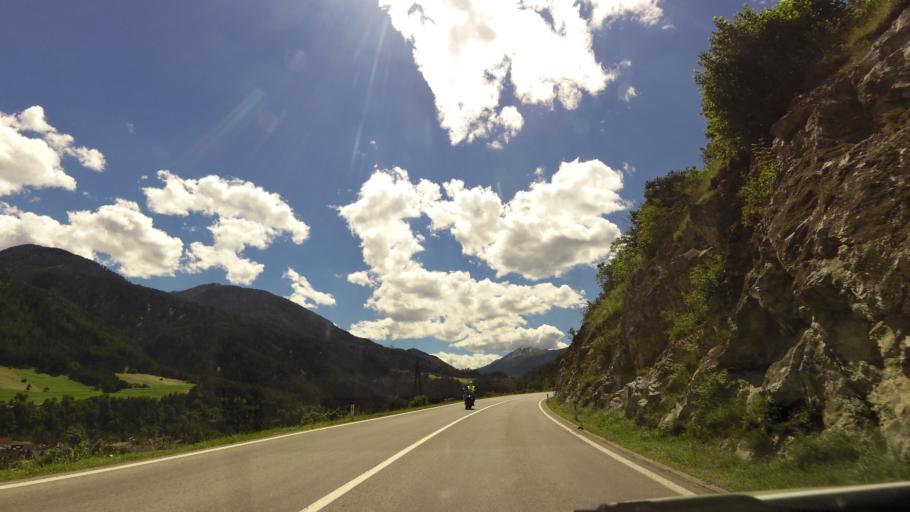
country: AT
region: Tyrol
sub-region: Politischer Bezirk Imst
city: Roppen
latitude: 47.2196
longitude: 10.8120
